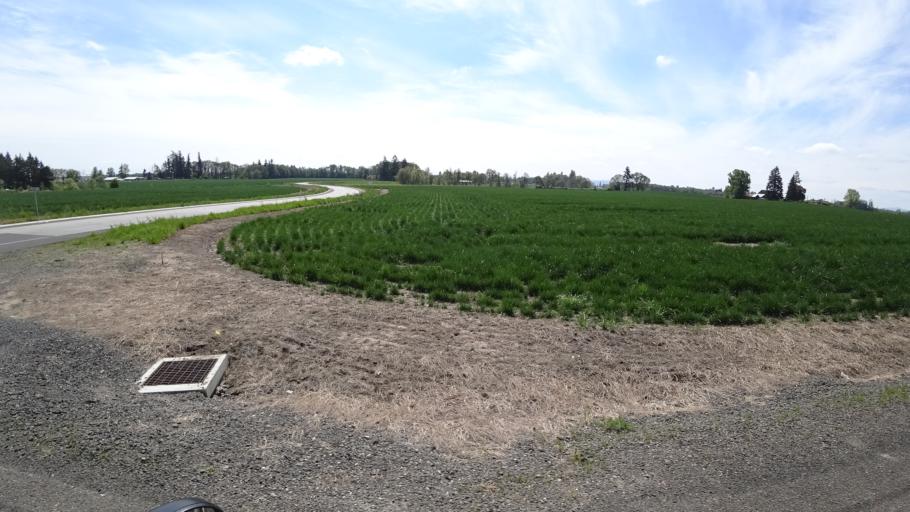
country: US
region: Oregon
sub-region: Washington County
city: Rockcreek
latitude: 45.5659
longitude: -122.9366
